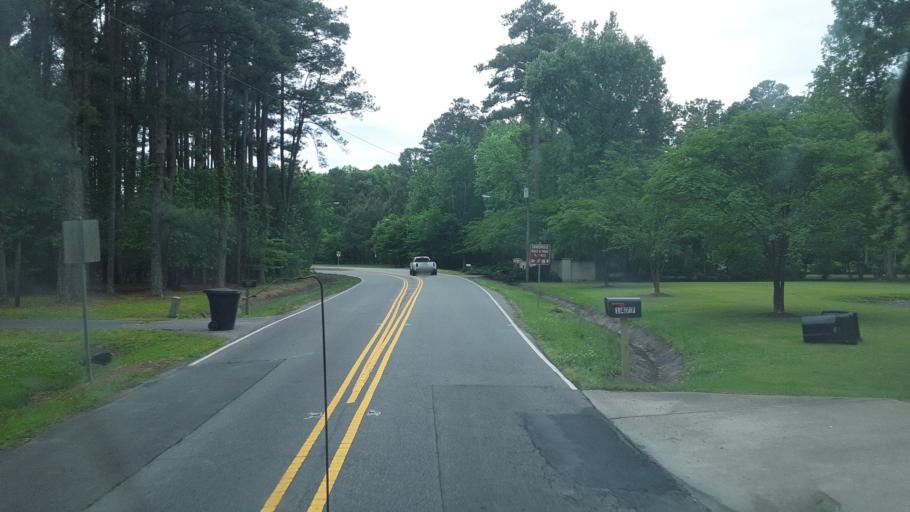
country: US
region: Virginia
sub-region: City of Virginia Beach
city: Virginia Beach
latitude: 36.7355
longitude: -75.9897
